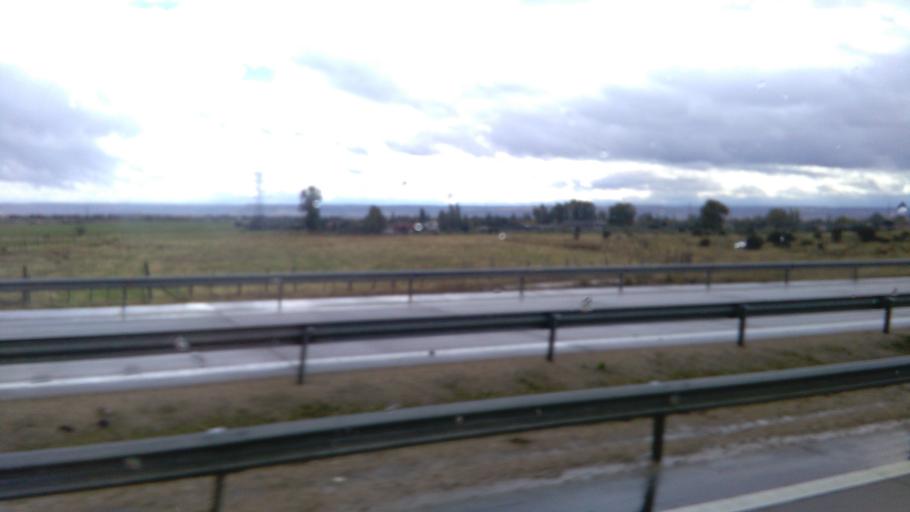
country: ES
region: Castille-La Mancha
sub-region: Province of Toledo
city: Cervera de los Montes
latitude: 40.0130
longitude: -4.8106
